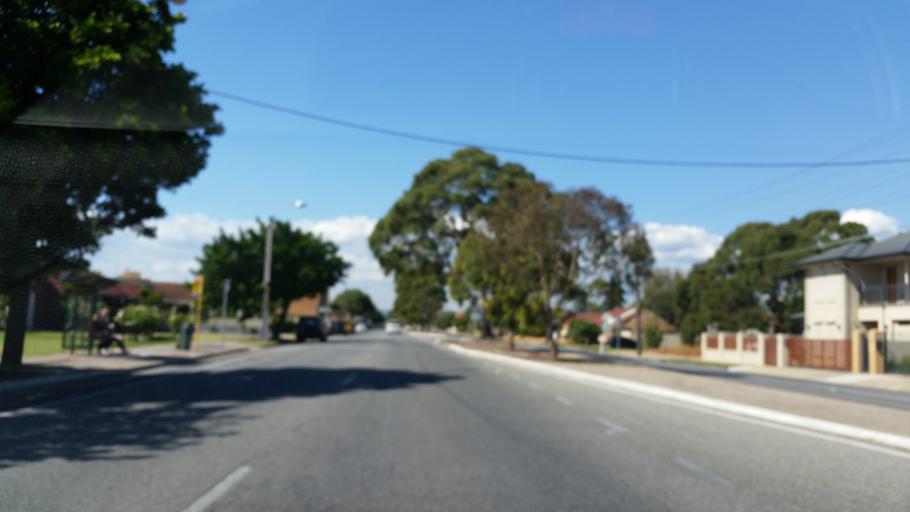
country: AU
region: South Australia
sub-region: Charles Sturt
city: Henley Beach
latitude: -34.9268
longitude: 138.5076
